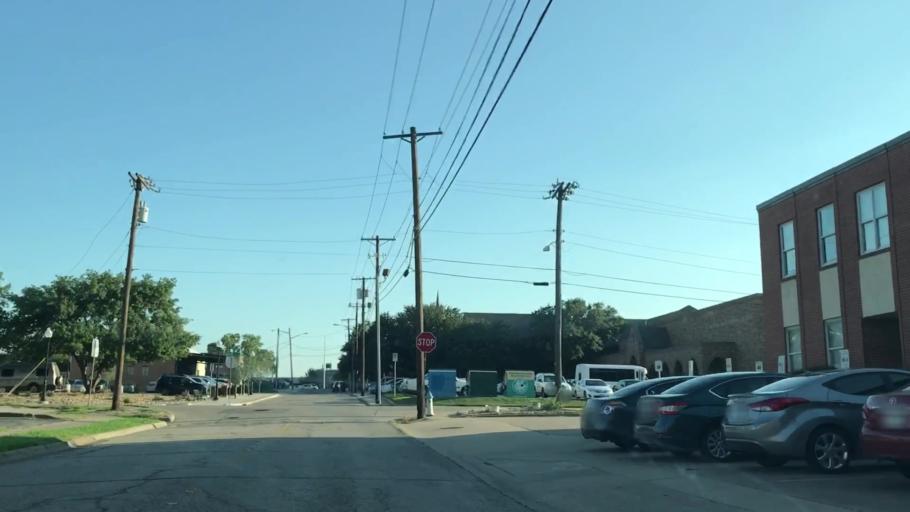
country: US
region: Texas
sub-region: Denton County
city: Denton
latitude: 33.2175
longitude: -97.1352
